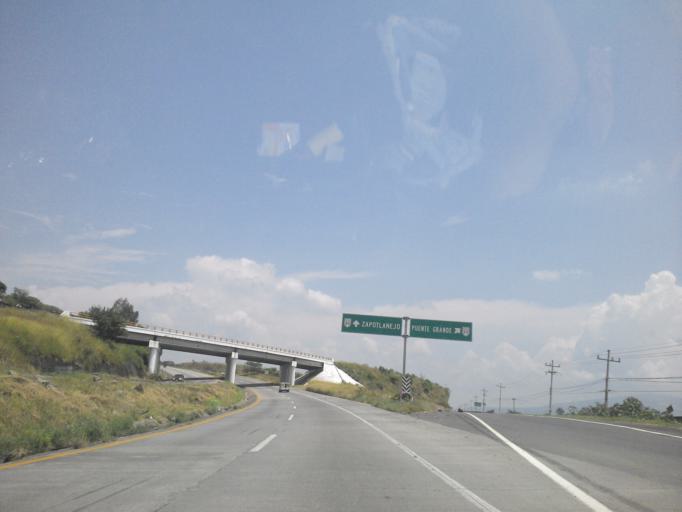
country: MX
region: Jalisco
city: Puente Grande
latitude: 20.5733
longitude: -103.1685
